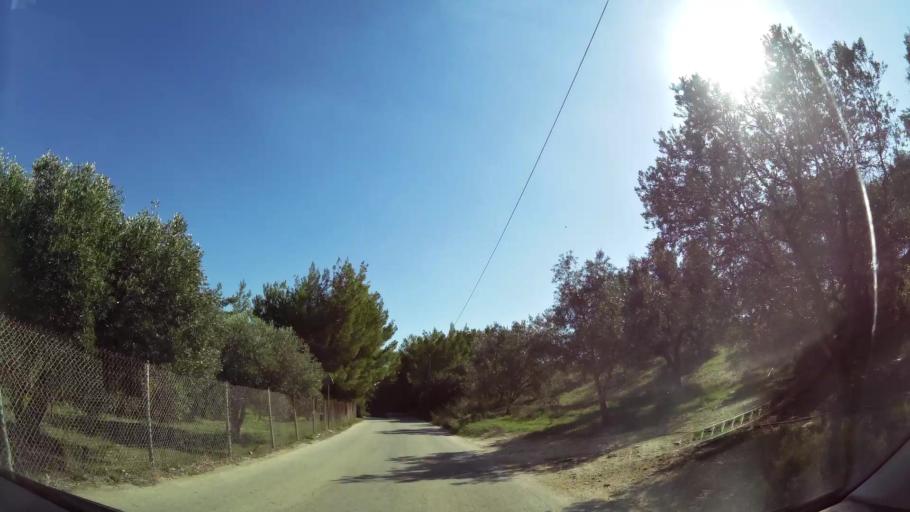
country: GR
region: Attica
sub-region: Nomarchia Anatolikis Attikis
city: Dioni
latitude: 38.0168
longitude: 23.9284
